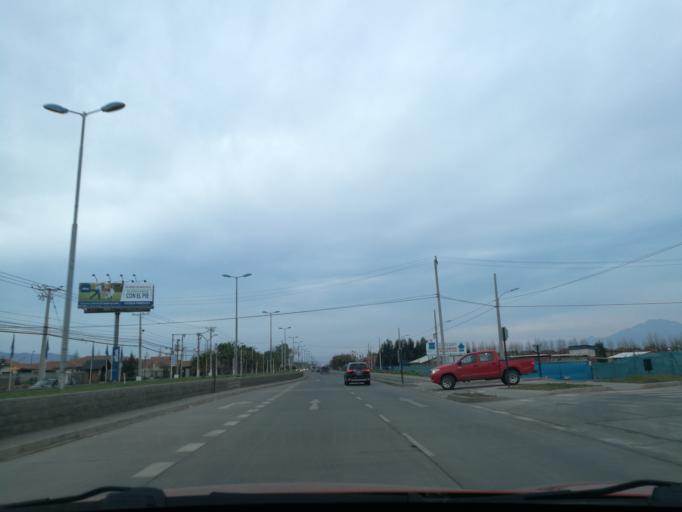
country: CL
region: O'Higgins
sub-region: Provincia de Cachapoal
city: Machali
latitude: -34.1694
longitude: -70.6780
